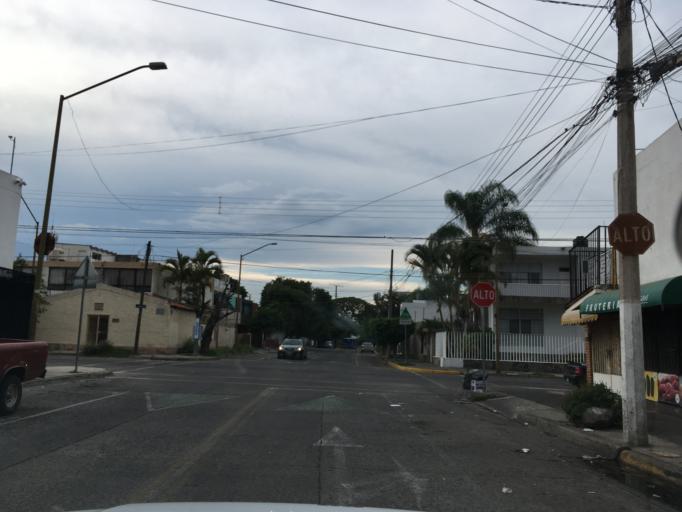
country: MX
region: Jalisco
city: Guadalajara
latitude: 20.6649
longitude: -103.3825
